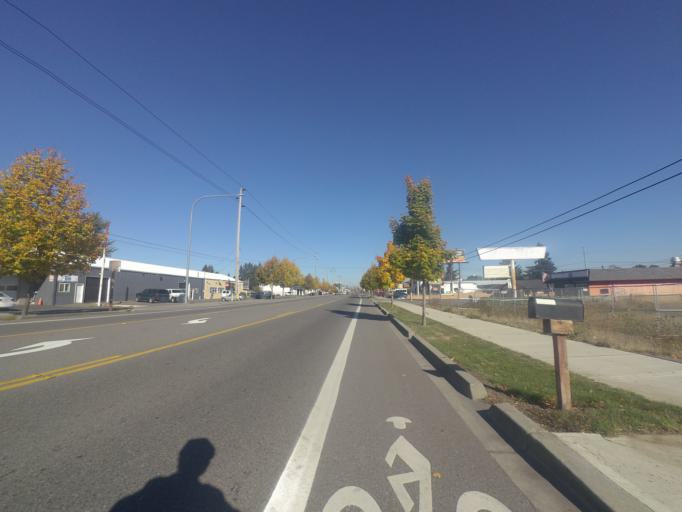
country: US
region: Washington
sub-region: Pierce County
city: McChord Air Force Base
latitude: 47.1473
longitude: -122.5078
